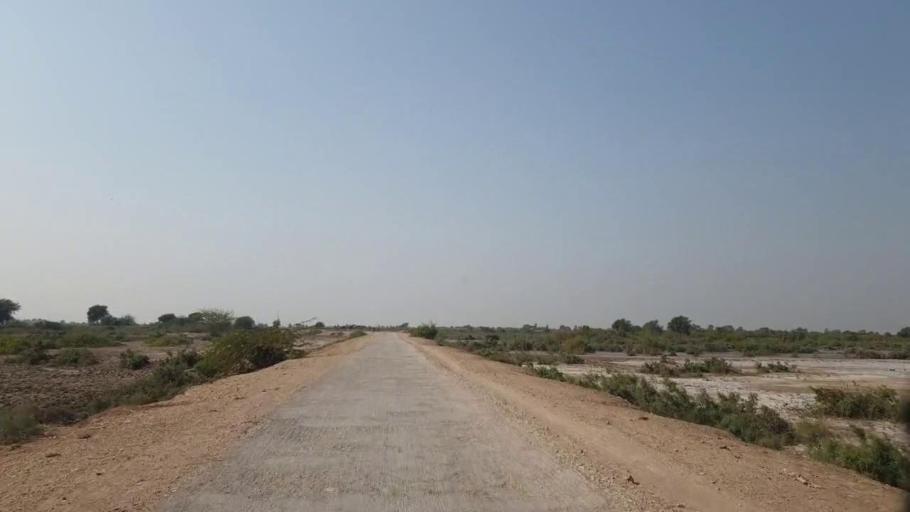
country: PK
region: Sindh
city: Bulri
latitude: 24.9572
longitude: 68.3532
